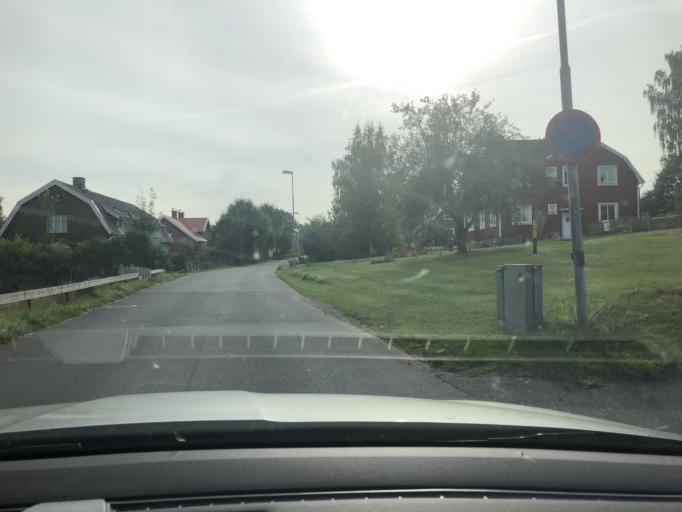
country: SE
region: Joenkoeping
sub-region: Vetlanda Kommun
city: Ekenassjon
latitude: 57.5206
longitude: 14.9096
